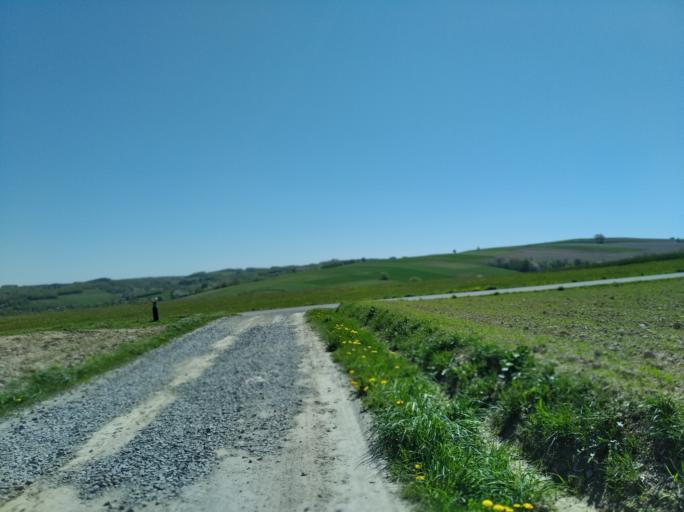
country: PL
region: Subcarpathian Voivodeship
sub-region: Powiat ropczycko-sedziszowski
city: Wielopole Skrzynskie
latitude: 49.9058
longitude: 21.5507
